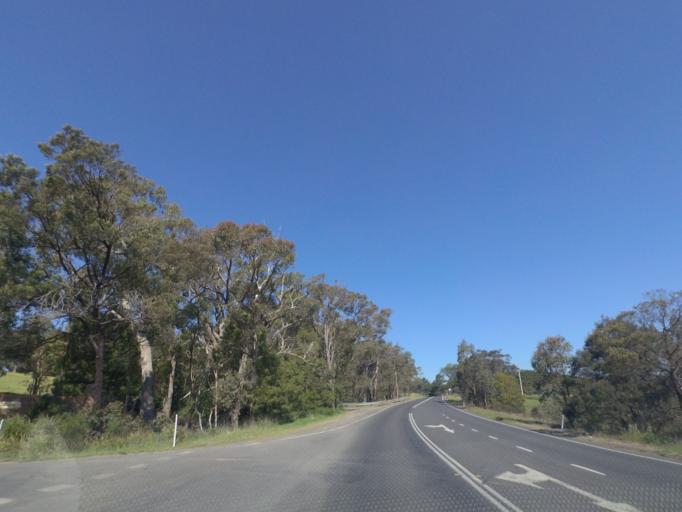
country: AU
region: Victoria
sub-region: Whittlesea
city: Whittlesea
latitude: -37.3453
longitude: 144.9984
